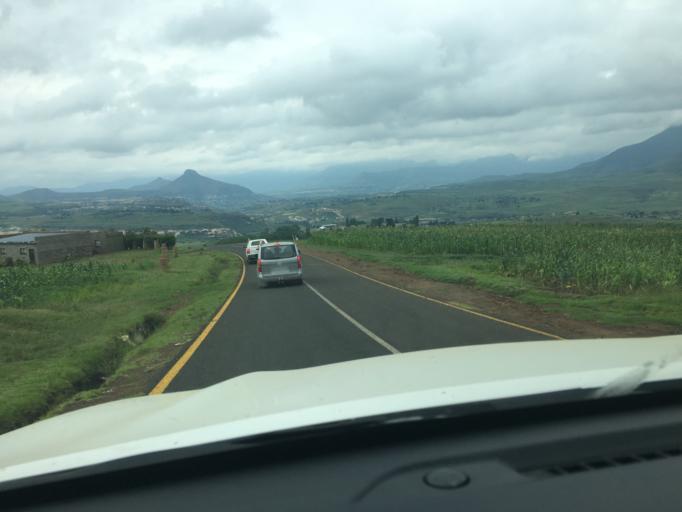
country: LS
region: Berea
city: Teyateyaneng
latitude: -29.2553
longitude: 27.8452
